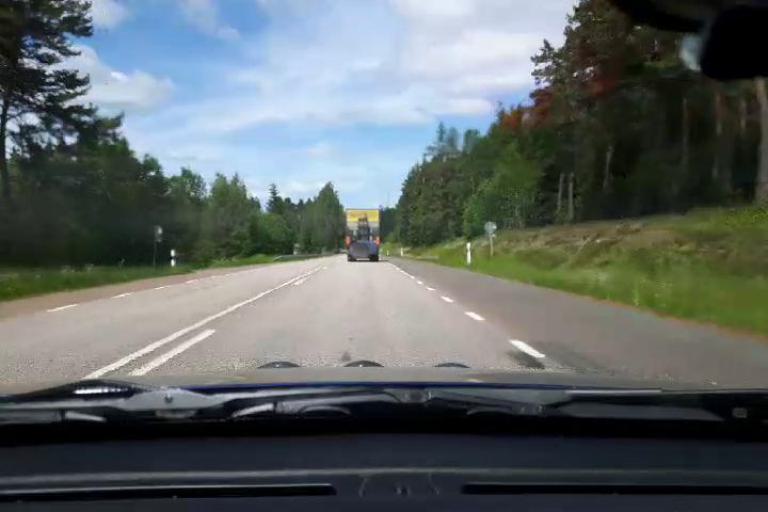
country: SE
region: Uppsala
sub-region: Osthammars Kommun
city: Bjorklinge
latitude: 60.0945
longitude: 17.5542
